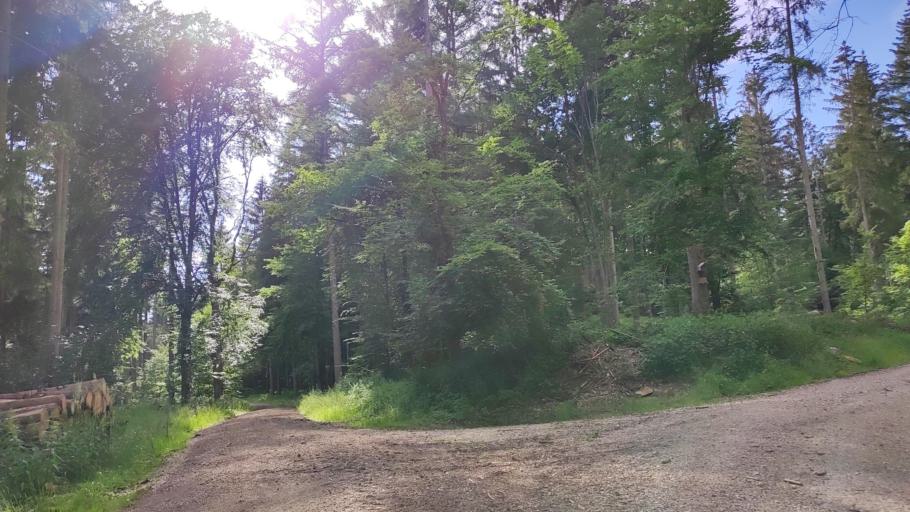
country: DE
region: Bavaria
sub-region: Swabia
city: Landensberg
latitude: 48.4262
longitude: 10.5658
